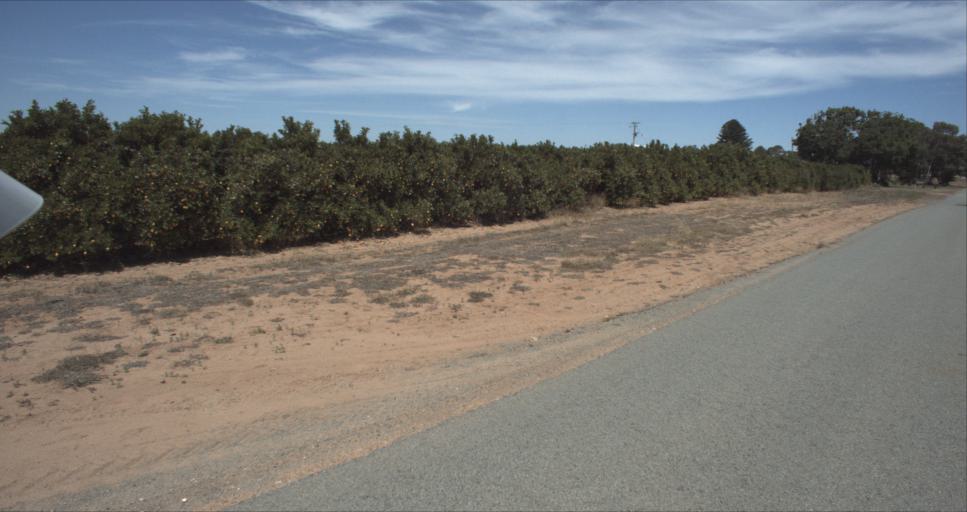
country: AU
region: New South Wales
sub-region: Leeton
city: Leeton
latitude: -34.6755
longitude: 146.4426
